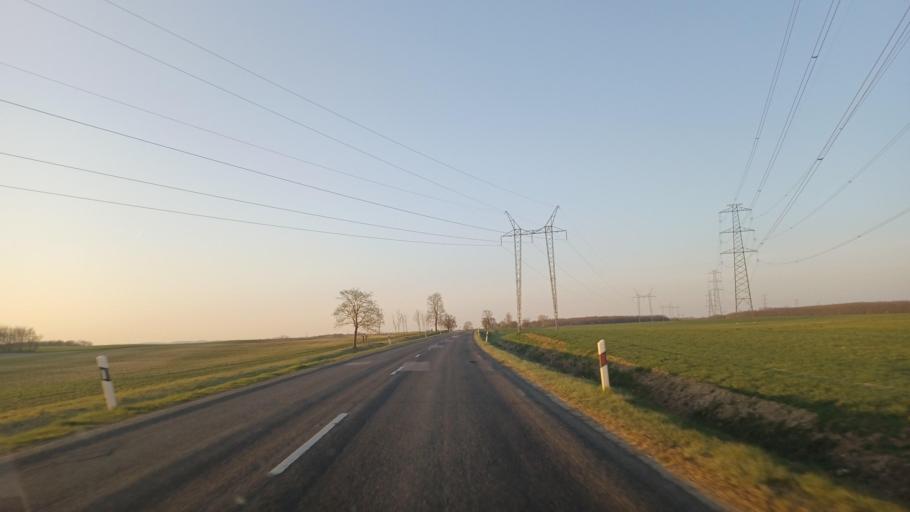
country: HU
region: Tolna
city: Szedres
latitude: 46.4472
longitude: 18.6869
